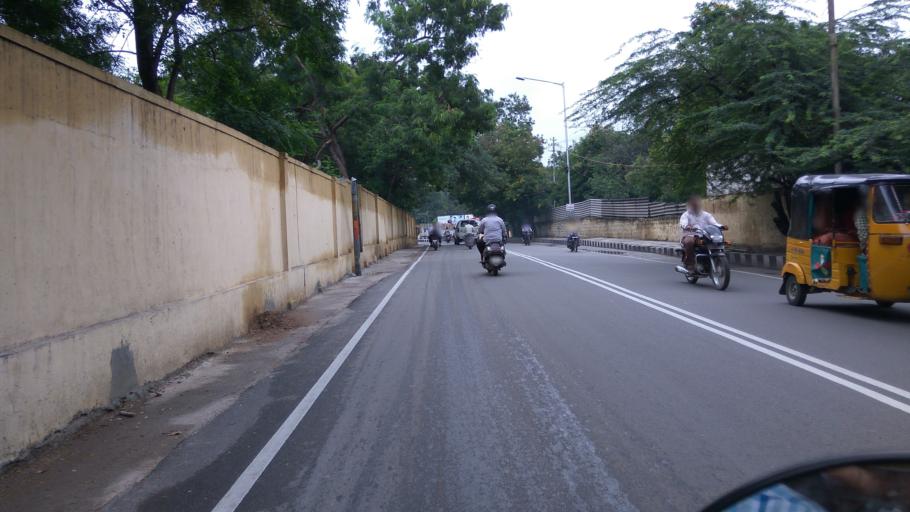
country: IN
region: Telangana
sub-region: Hyderabad
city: Malkajgiri
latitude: 17.4369
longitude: 78.5231
